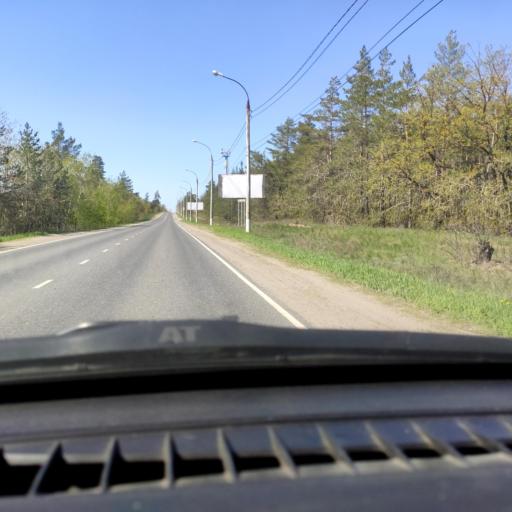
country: RU
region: Samara
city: Tol'yatti
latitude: 53.4762
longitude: 49.4197
